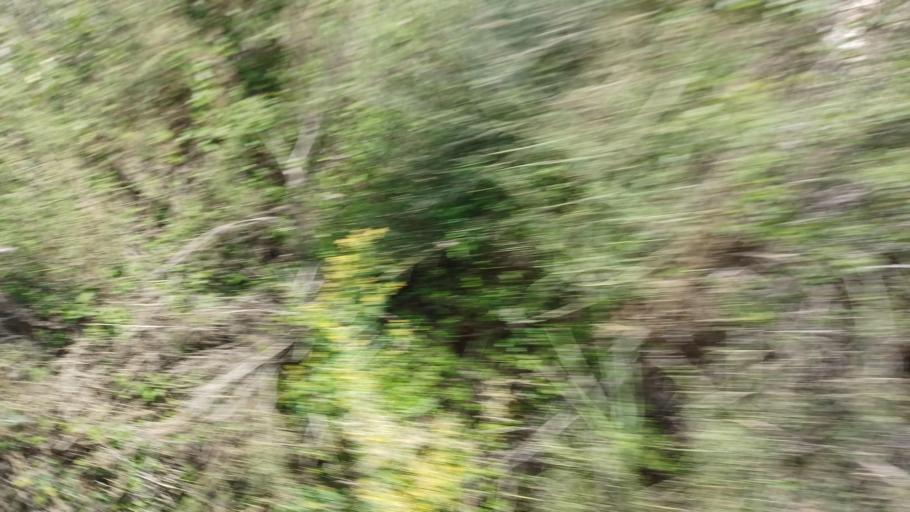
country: CY
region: Limassol
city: Pissouri
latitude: 34.7620
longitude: 32.6421
